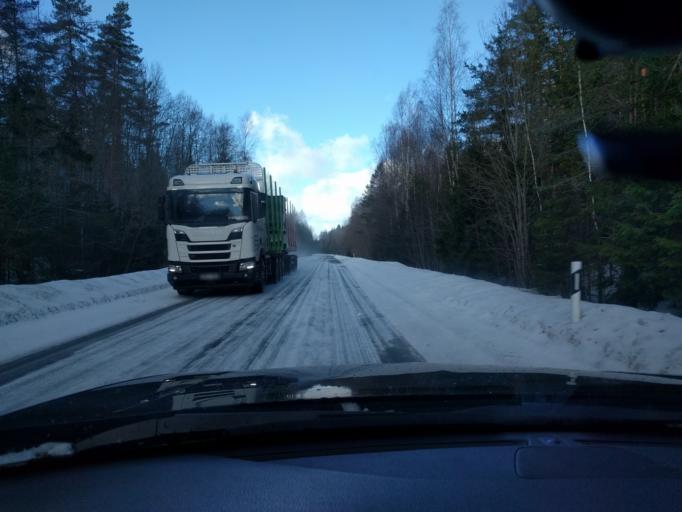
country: EE
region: Harju
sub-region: Anija vald
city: Kehra
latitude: 59.2175
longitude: 25.4812
